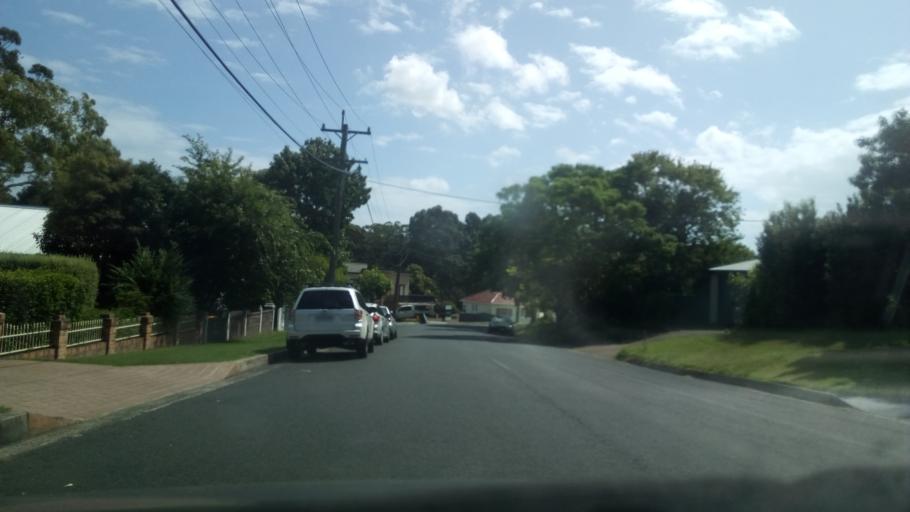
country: AU
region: New South Wales
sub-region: Wollongong
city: Keiraville
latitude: -34.4213
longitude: 150.8766
